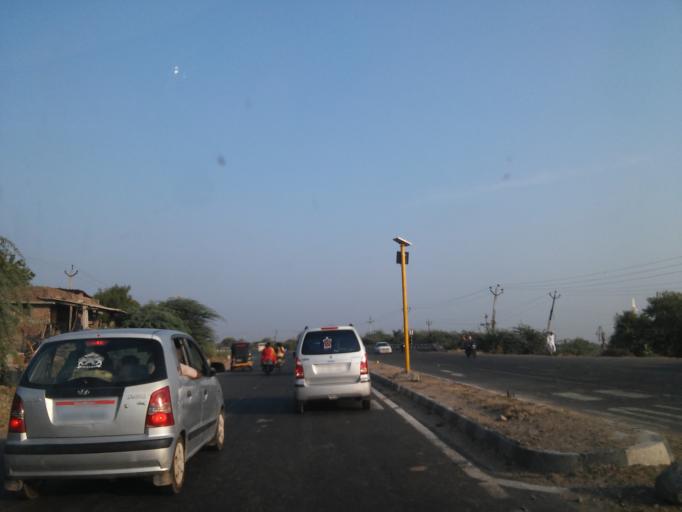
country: IN
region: Gujarat
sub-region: Ahmadabad
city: Sanand
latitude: 23.0832
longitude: 72.1361
